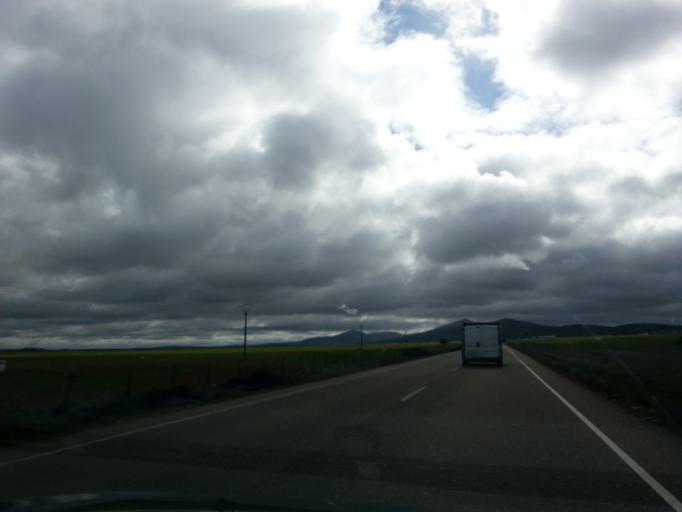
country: ES
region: Castille and Leon
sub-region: Provincia de Salamanca
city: Tamames
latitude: 40.6766
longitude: -6.1254
